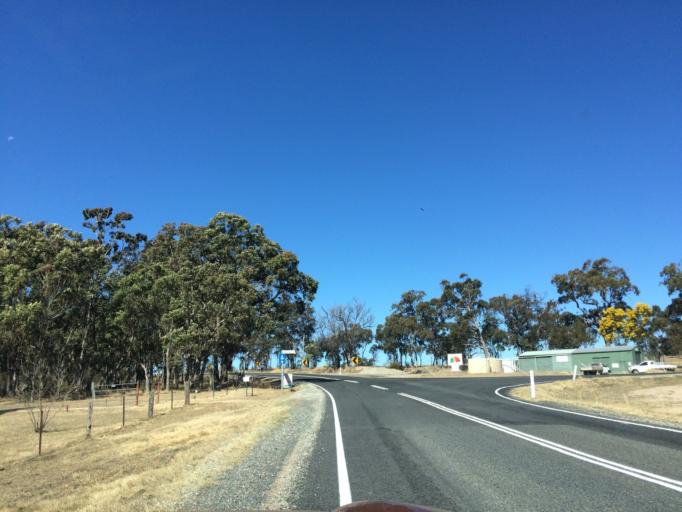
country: AU
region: Queensland
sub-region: Southern Downs
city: Stanthorpe
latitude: -28.6963
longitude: 152.0033
